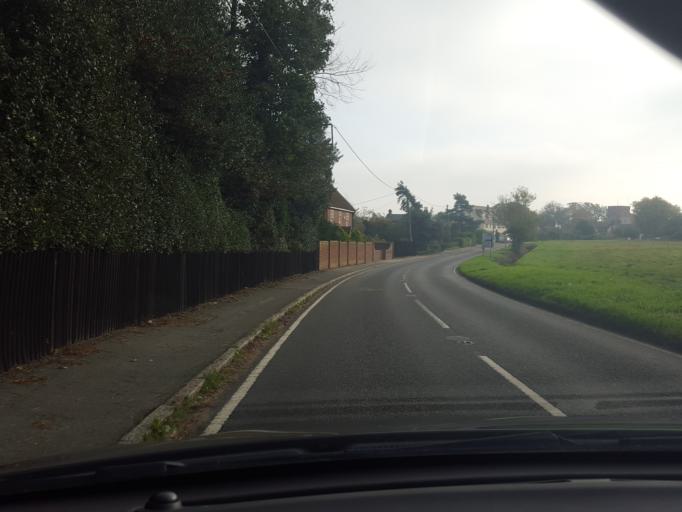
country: GB
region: England
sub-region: Essex
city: Mistley
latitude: 51.9368
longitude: 1.1149
